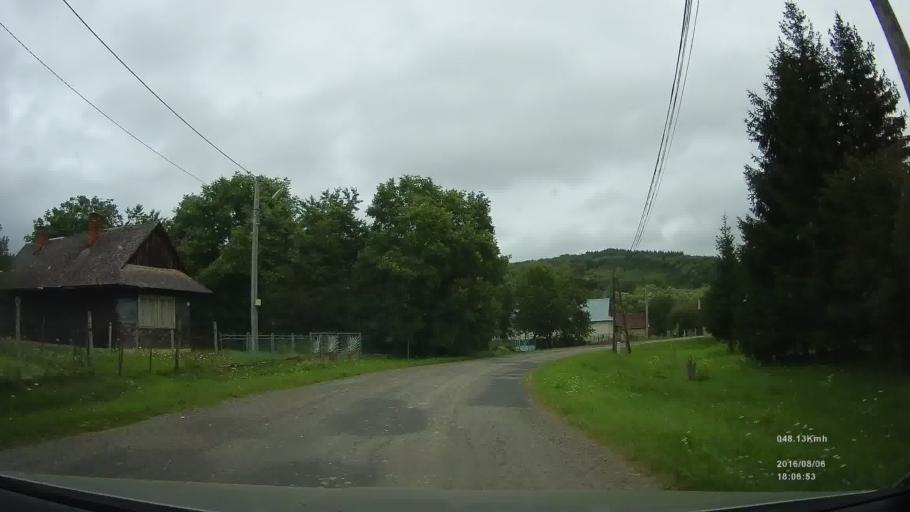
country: SK
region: Presovsky
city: Svidnik
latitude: 49.4004
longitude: 21.5705
